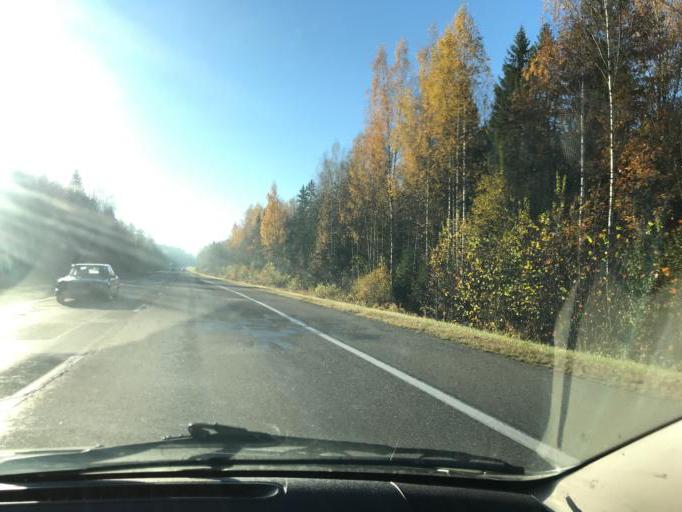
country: BY
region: Vitebsk
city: Vitebsk
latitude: 54.8962
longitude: 30.3790
